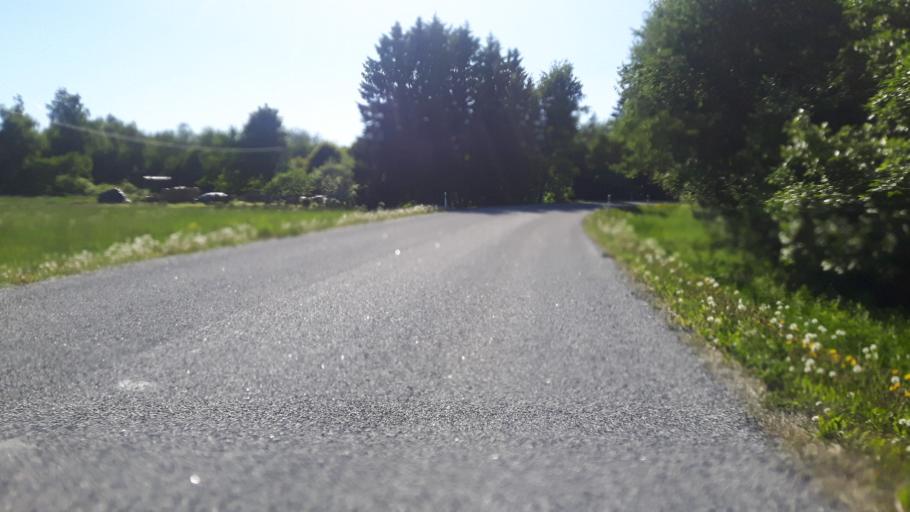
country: EE
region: Ida-Virumaa
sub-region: Kohtla-Jaerve linn
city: Kohtla-Jarve
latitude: 59.4388
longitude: 27.2790
